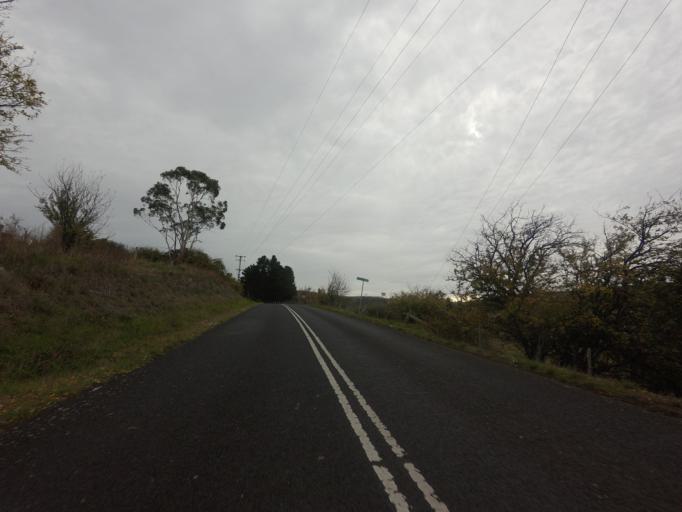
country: AU
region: Tasmania
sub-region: Derwent Valley
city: New Norfolk
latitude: -42.6043
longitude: 147.0770
